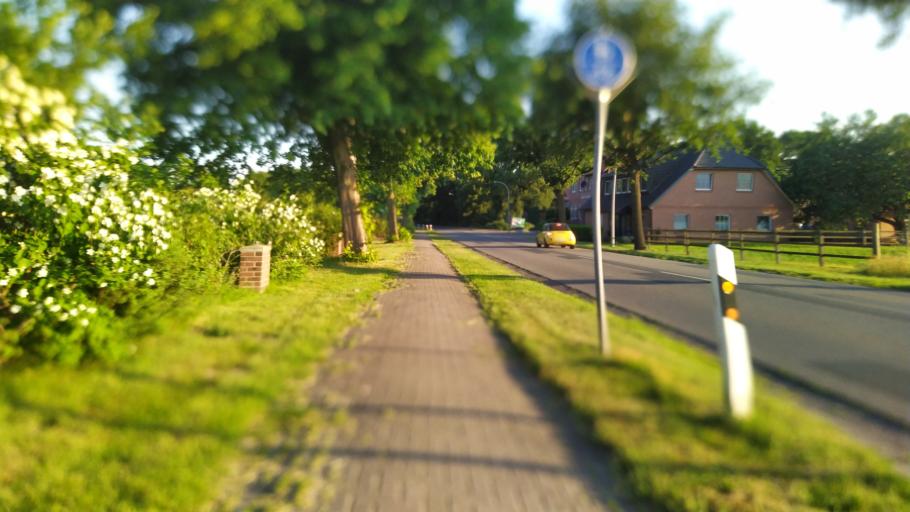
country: DE
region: Lower Saxony
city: Ebersdorf
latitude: 53.5297
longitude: 9.0525
